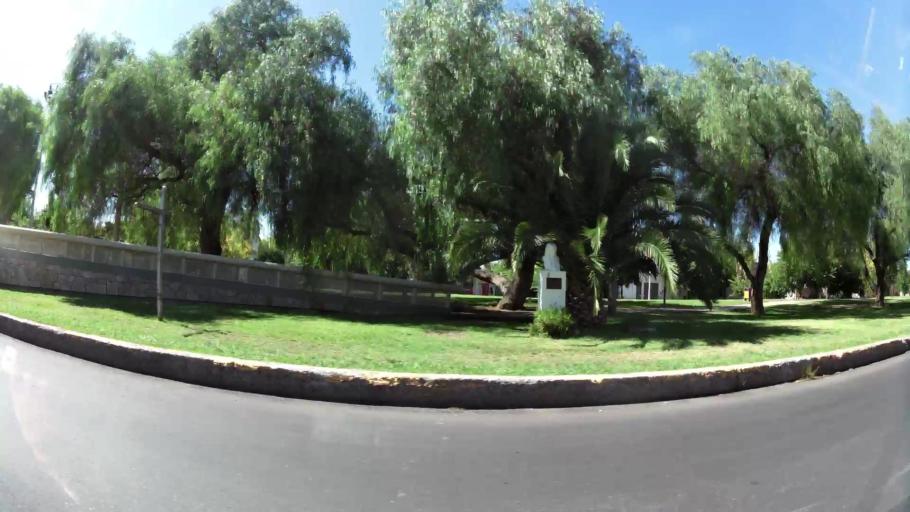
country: AR
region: Mendoza
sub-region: Departamento de Godoy Cruz
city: Godoy Cruz
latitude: -32.9426
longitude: -68.8506
